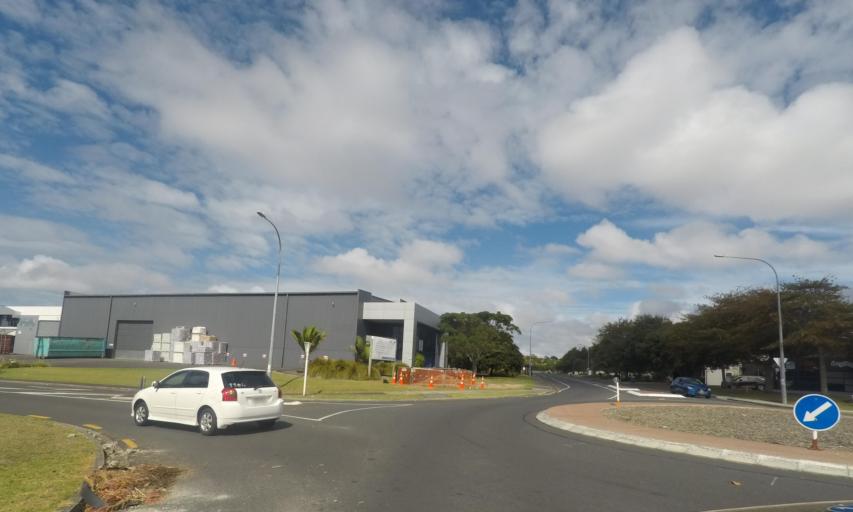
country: NZ
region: Auckland
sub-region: Auckland
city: Rothesay Bay
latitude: -36.7467
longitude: 174.6985
